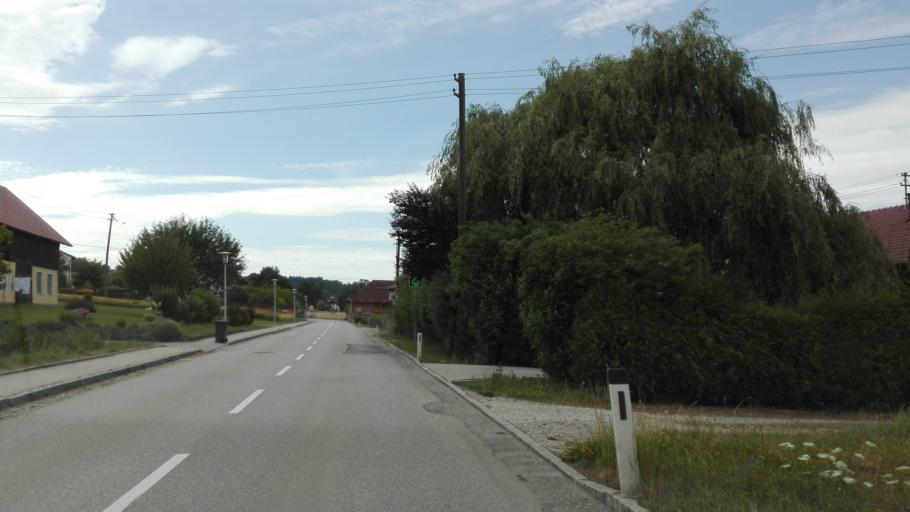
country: AT
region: Upper Austria
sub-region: Politischer Bezirk Grieskirchen
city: Grieskirchen
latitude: 48.2428
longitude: 13.8194
